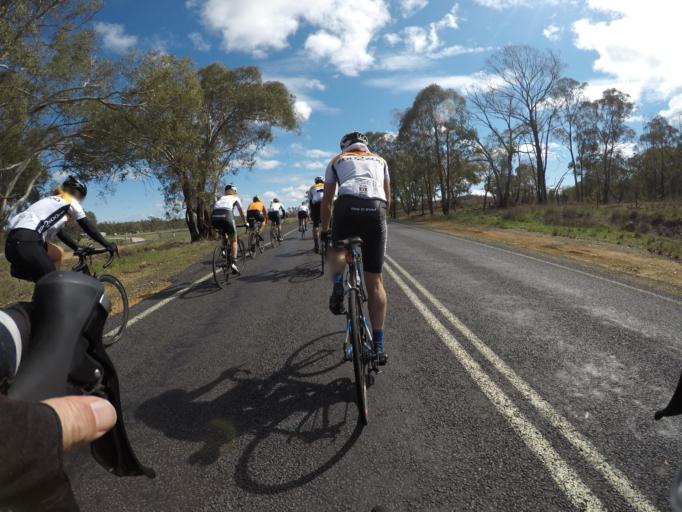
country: AU
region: New South Wales
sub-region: Parkes
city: Peak Hill
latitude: -32.7049
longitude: 148.5531
